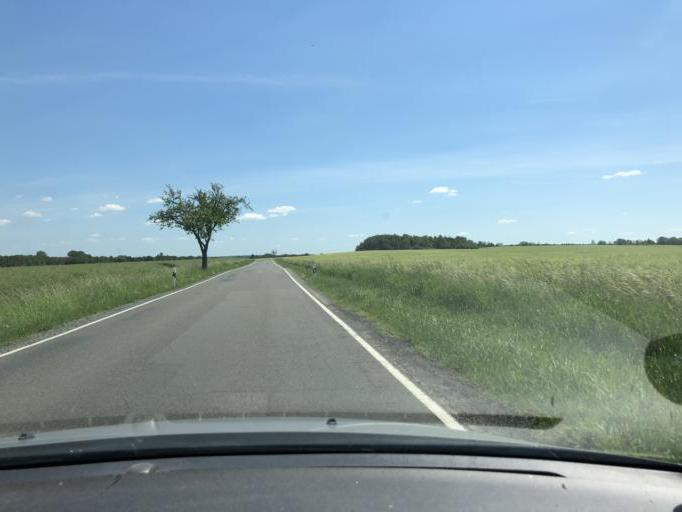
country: DE
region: Saxony
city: Trebsen
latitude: 51.2895
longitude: 12.7076
